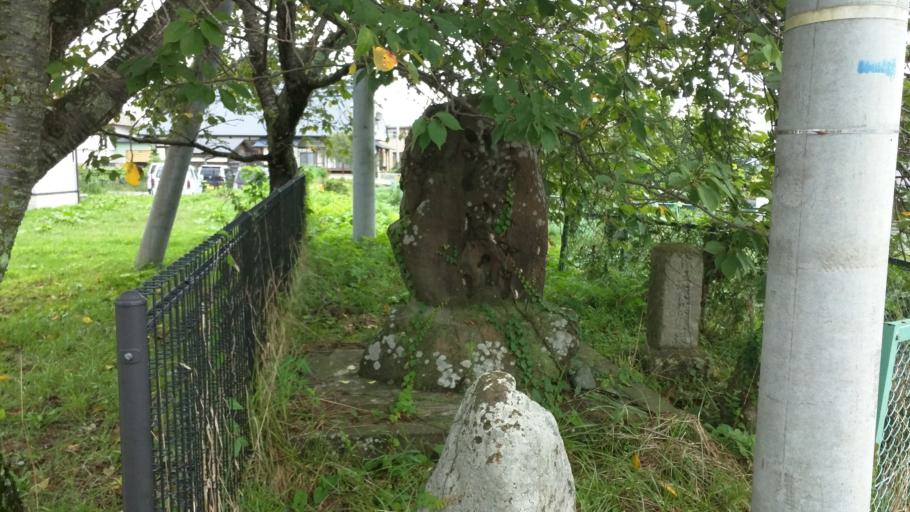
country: JP
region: Fukushima
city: Kitakata
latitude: 37.5096
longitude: 139.8324
